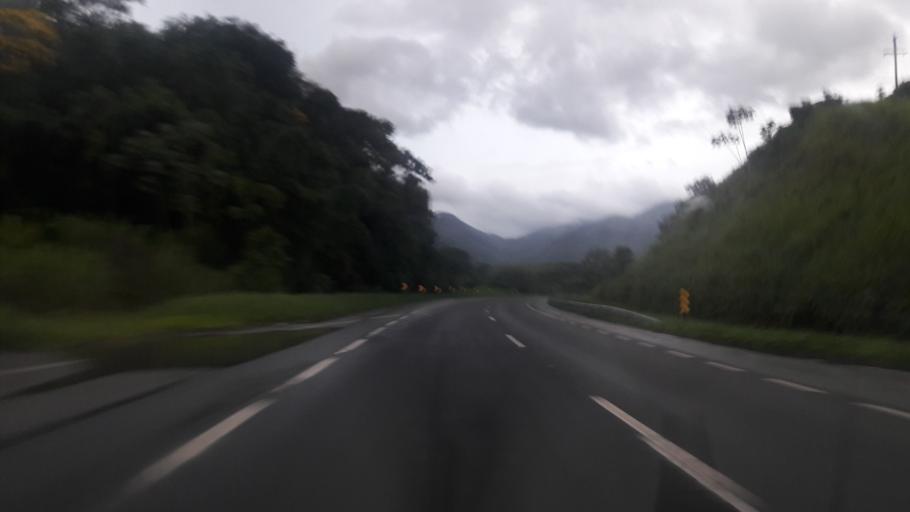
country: BR
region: Sao Paulo
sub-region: Cajati
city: Cajati
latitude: -24.7791
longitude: -48.1953
